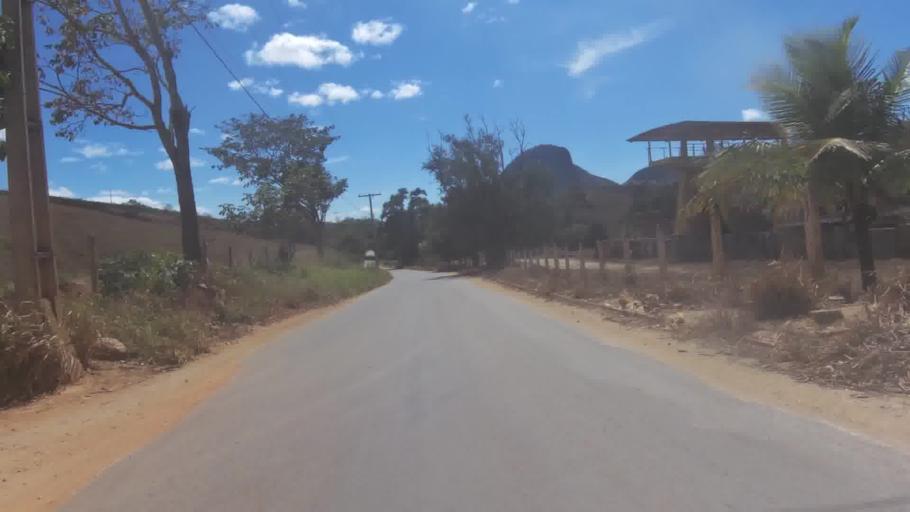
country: BR
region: Espirito Santo
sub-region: Cachoeiro De Itapemirim
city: Cachoeiro de Itapemirim
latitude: -20.9270
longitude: -41.2121
